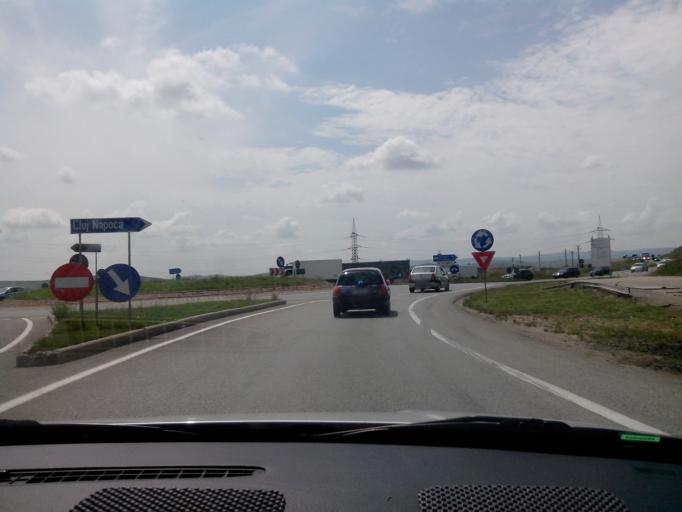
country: RO
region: Cluj
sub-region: Comuna Apahida
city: Apahida
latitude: 46.8228
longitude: 23.7444
